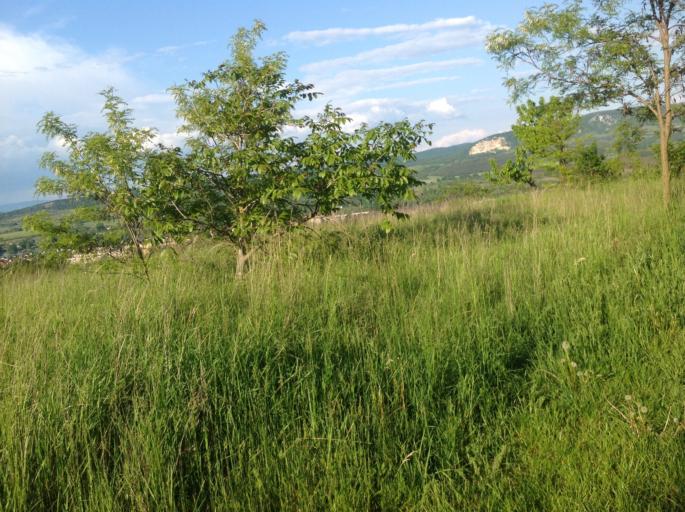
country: HU
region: Komarom-Esztergom
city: Dorog
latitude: 47.7154
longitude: 18.7275
